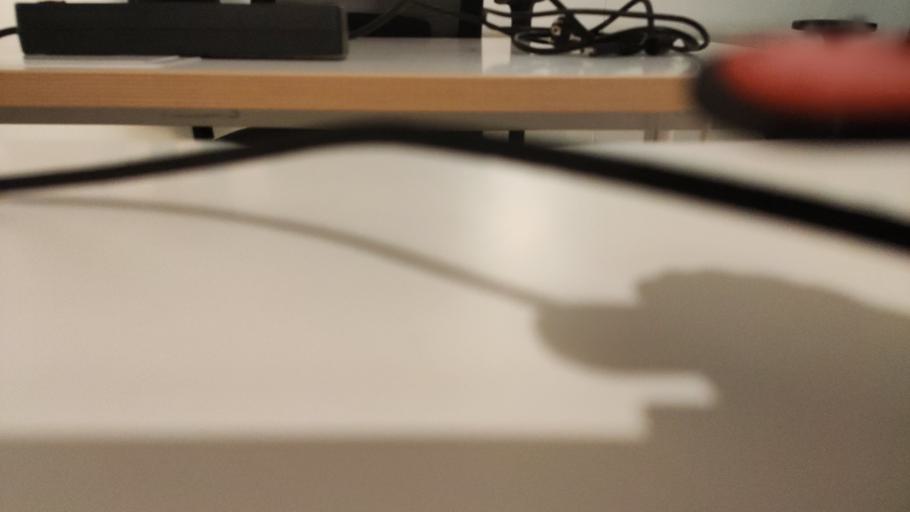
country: RU
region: Moskovskaya
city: Proletarskiy
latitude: 54.9757
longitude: 37.3587
